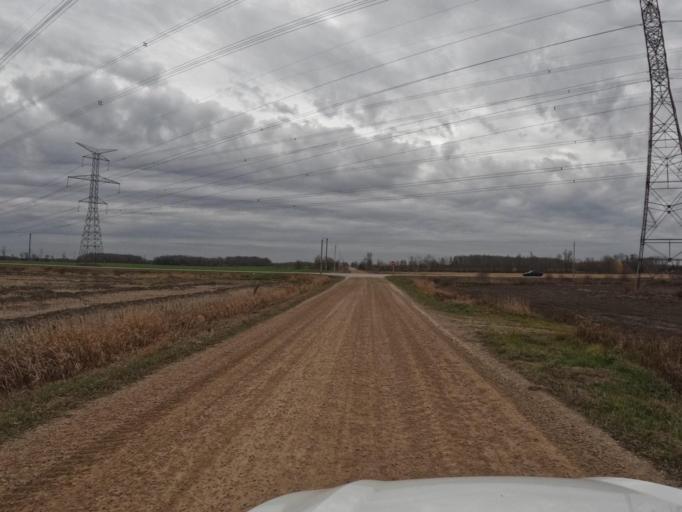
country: CA
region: Ontario
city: Shelburne
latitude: 43.9874
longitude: -80.3840
